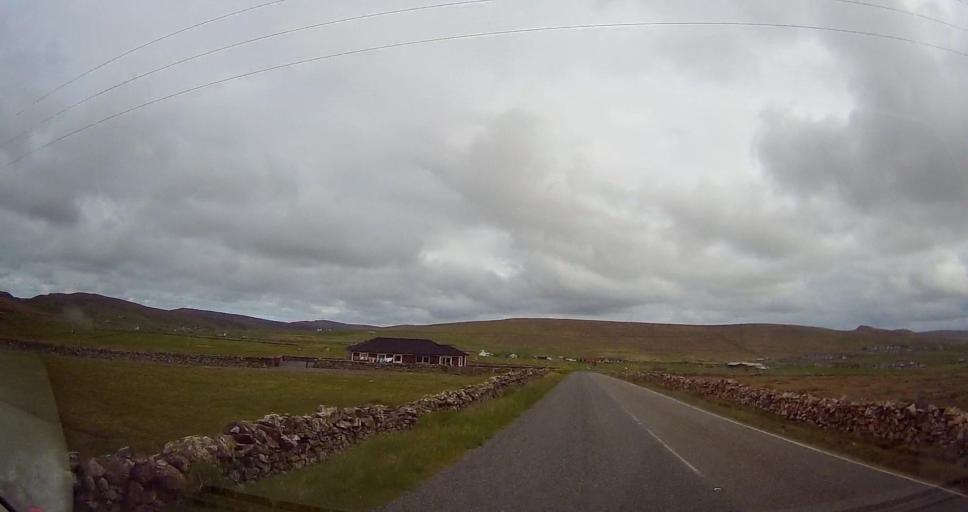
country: GB
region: Scotland
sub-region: Shetland Islands
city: Shetland
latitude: 60.7524
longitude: -0.8847
